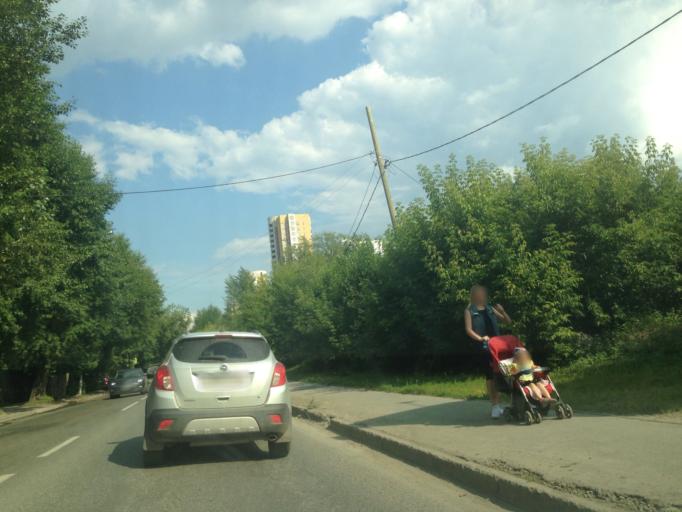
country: RU
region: Sverdlovsk
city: Yekaterinburg
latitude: 56.8669
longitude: 60.6349
